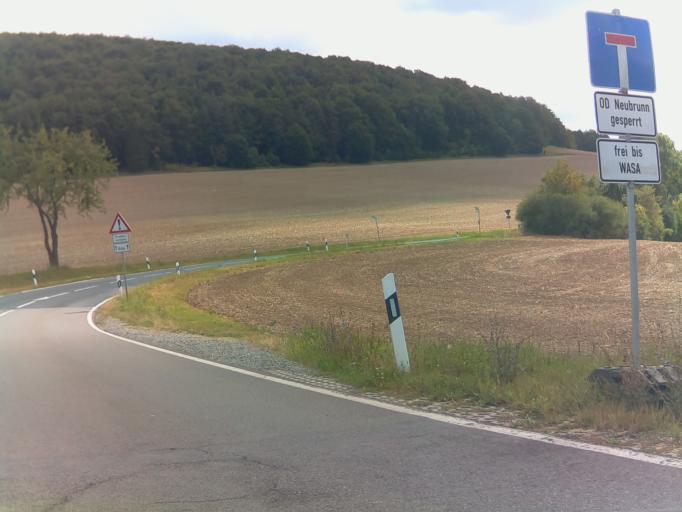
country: DE
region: Thuringia
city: Ritschenhausen
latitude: 50.5206
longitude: 10.4329
